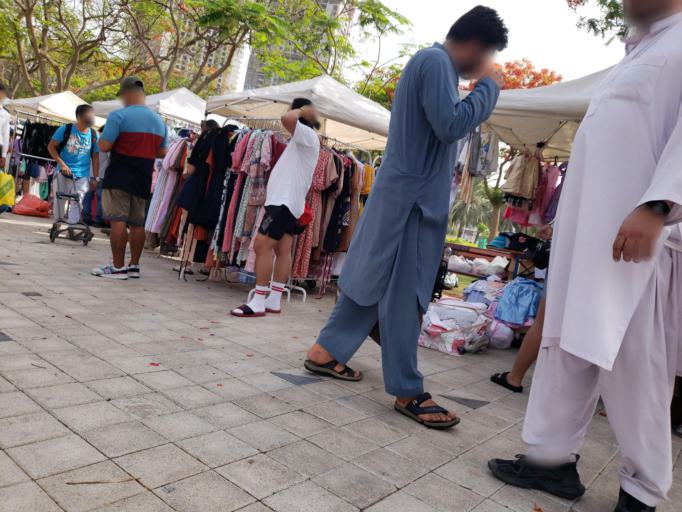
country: AE
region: Ash Shariqah
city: Sharjah
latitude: 25.2363
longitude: 55.2966
